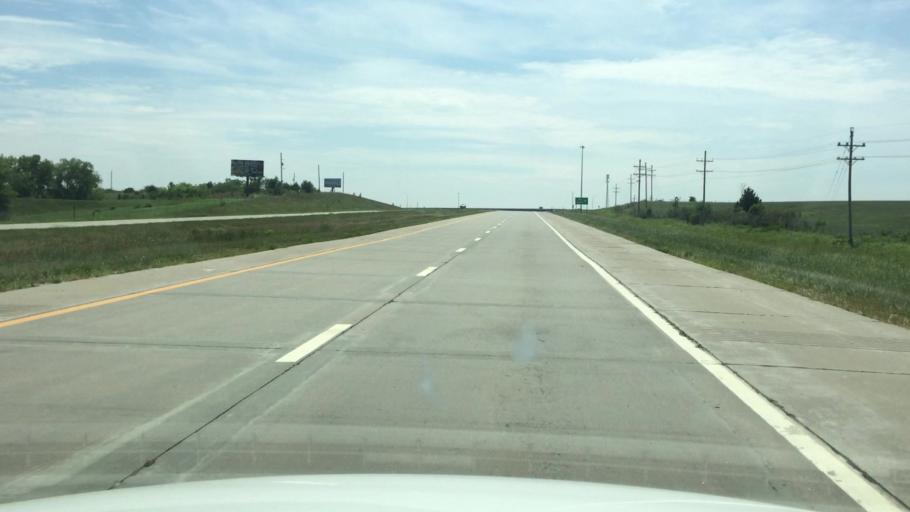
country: US
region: Kansas
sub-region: Jackson County
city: Holton
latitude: 39.3252
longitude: -95.7201
